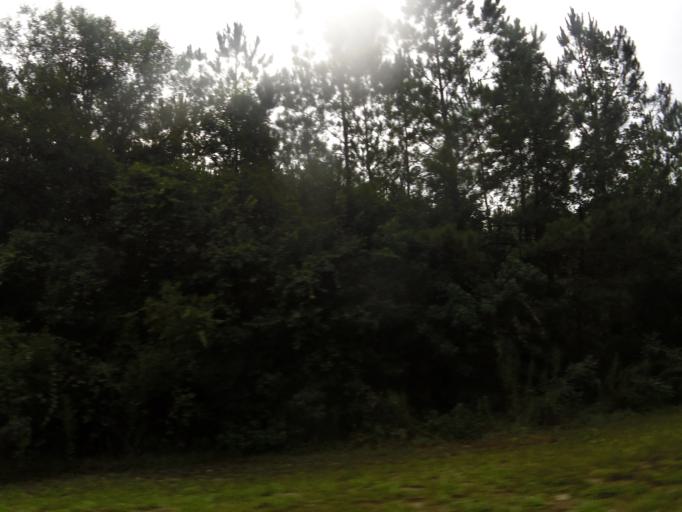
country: US
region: Florida
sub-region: Duval County
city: Jacksonville Beach
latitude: 30.2648
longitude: -81.5002
